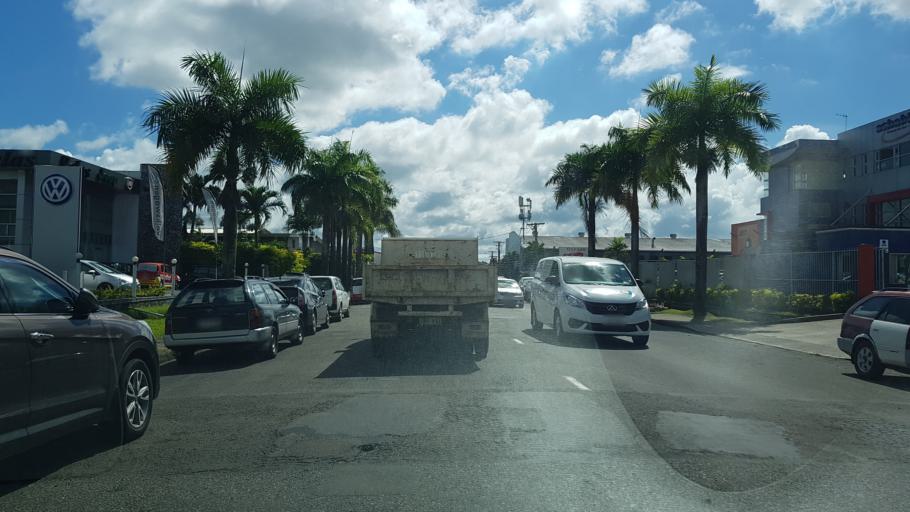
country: FJ
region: Central
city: Suva
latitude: -18.1277
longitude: 178.4550
